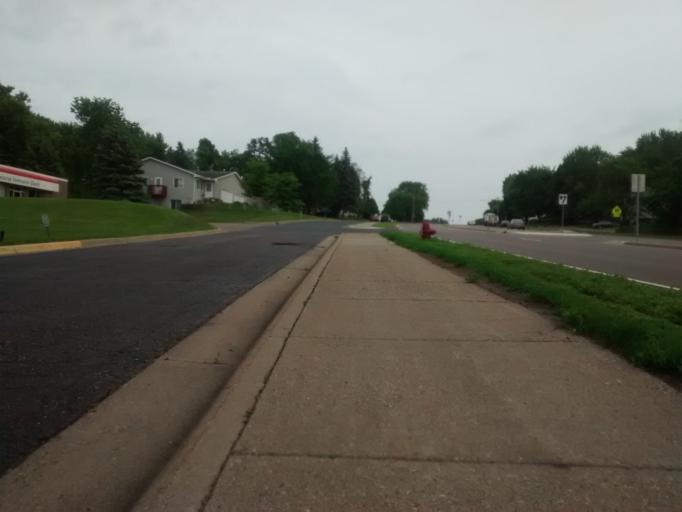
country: US
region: Minnesota
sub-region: Dakota County
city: Burnsville
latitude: 44.7686
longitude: -93.3040
